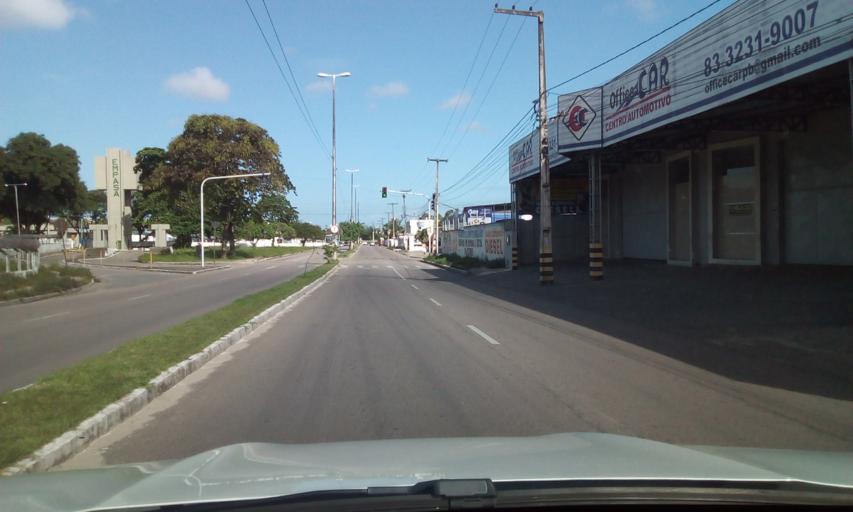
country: BR
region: Paraiba
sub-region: Joao Pessoa
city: Joao Pessoa
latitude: -7.1660
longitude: -34.8667
